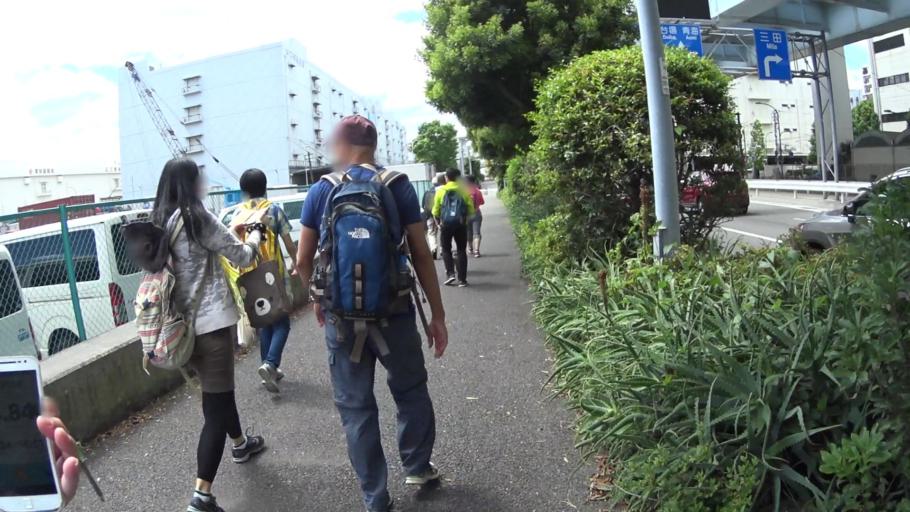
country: JP
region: Tokyo
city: Tokyo
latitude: 35.6427
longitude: 139.7601
